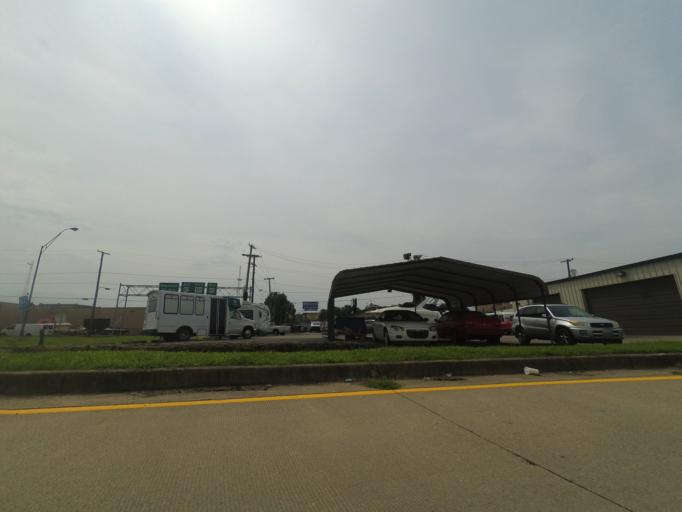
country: US
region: West Virginia
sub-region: Cabell County
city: Huntington
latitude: 38.4206
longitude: -82.4512
